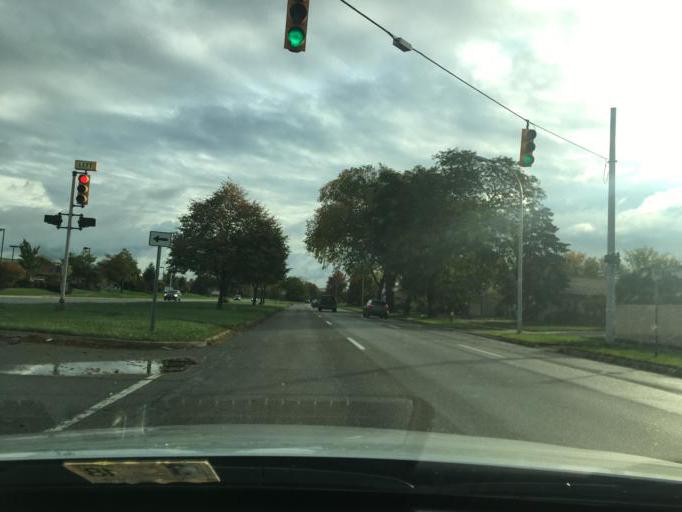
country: US
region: Michigan
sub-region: Wayne County
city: Allen Park
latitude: 42.2777
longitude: -83.2130
